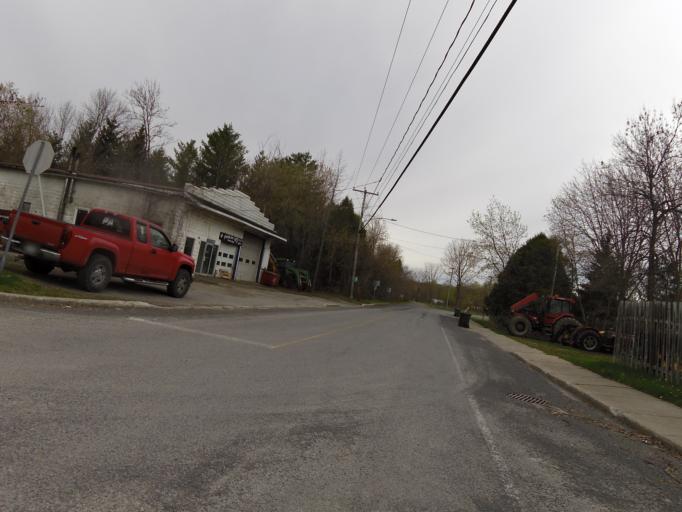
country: CA
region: Quebec
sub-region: Monteregie
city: Hudson
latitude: 45.5281
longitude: -74.2087
